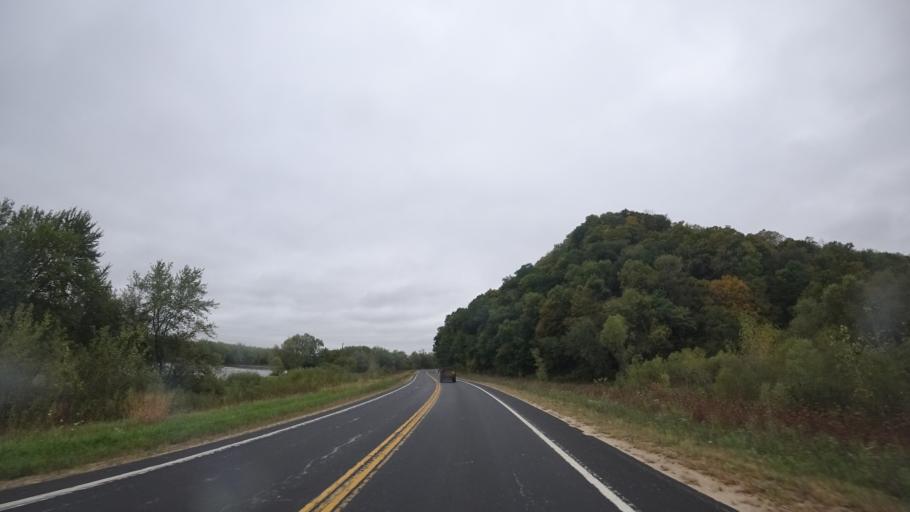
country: US
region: Wisconsin
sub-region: Grant County
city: Boscobel
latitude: 43.1372
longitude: -90.7427
